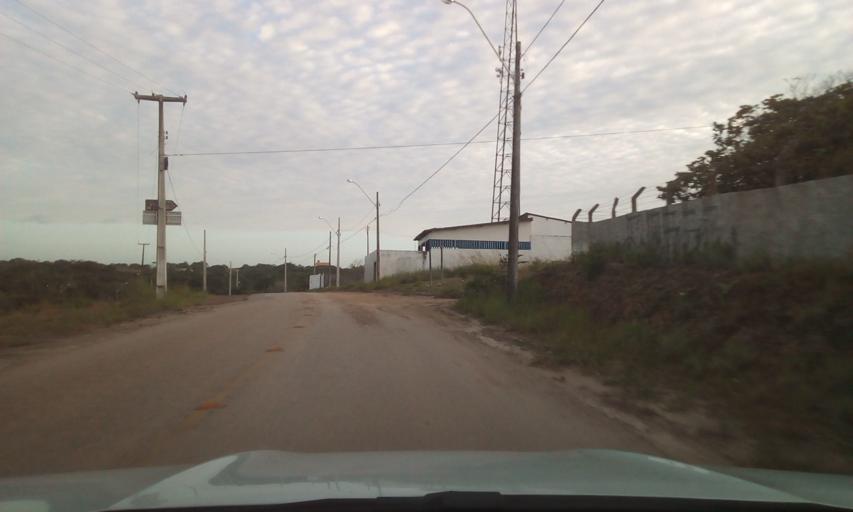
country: BR
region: Paraiba
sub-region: Conde
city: Conde
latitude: -7.2185
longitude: -34.8106
